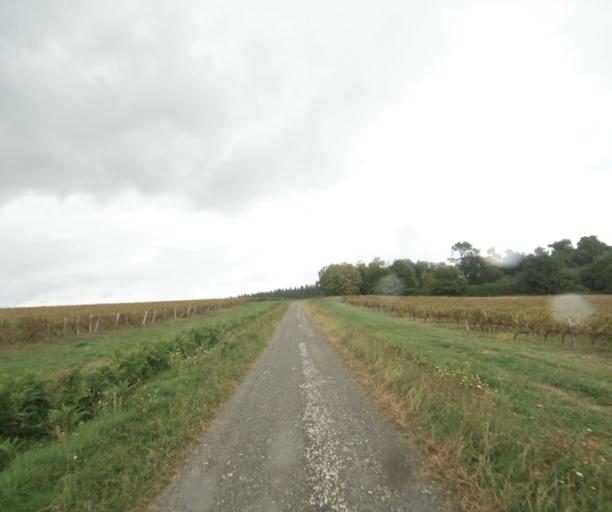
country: FR
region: Midi-Pyrenees
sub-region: Departement du Gers
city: Eauze
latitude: 43.8778
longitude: 0.0714
